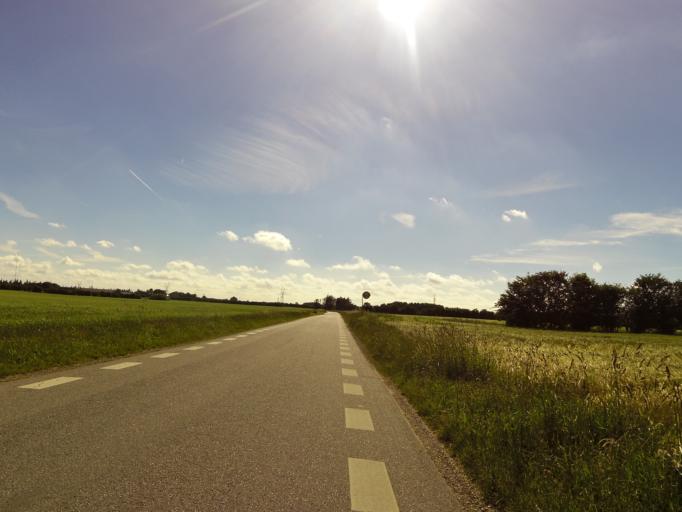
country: DK
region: South Denmark
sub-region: Aabenraa Kommune
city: Rodekro
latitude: 55.0690
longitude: 9.2830
